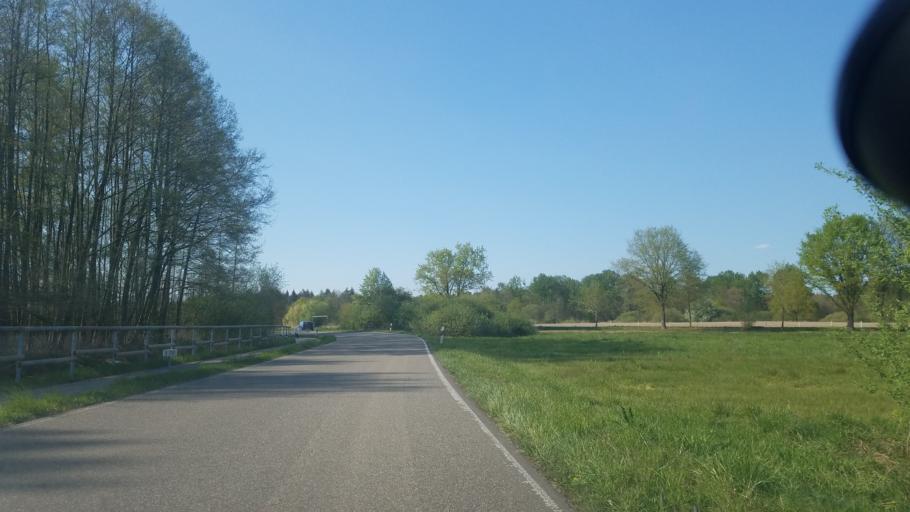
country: DE
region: Baden-Wuerttemberg
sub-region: Karlsruhe Region
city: Hugelsheim
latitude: 48.7689
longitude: 8.1112
